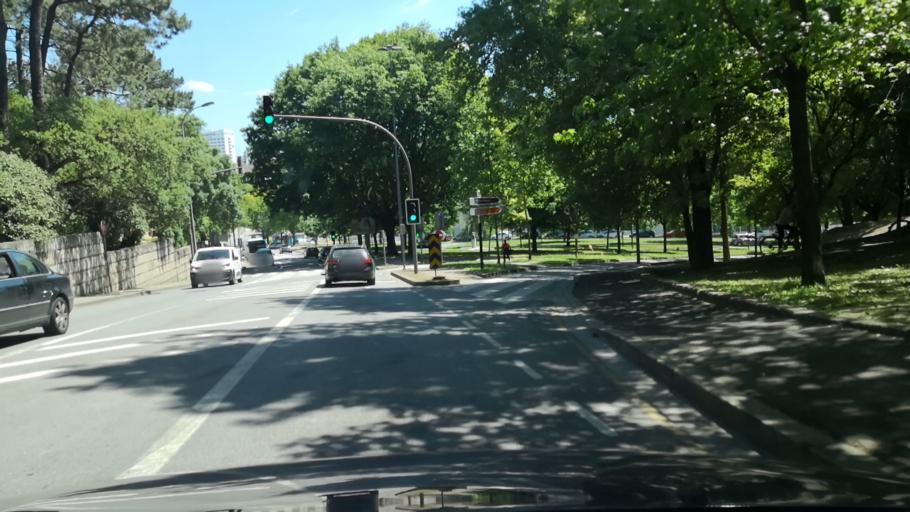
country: PT
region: Porto
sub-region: Vila Nova de Gaia
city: Canidelo
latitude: 41.1510
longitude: -8.6578
